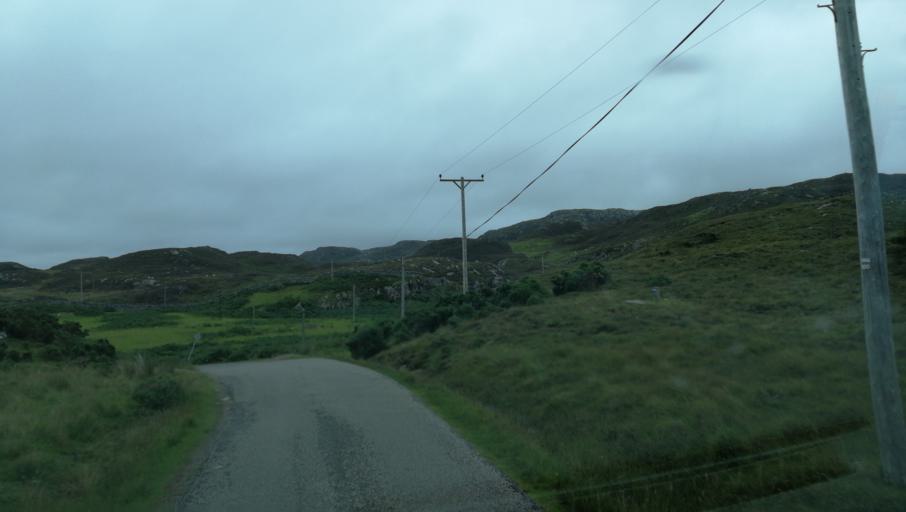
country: GB
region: Scotland
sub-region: Highland
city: Ullapool
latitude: 58.1303
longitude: -5.2571
